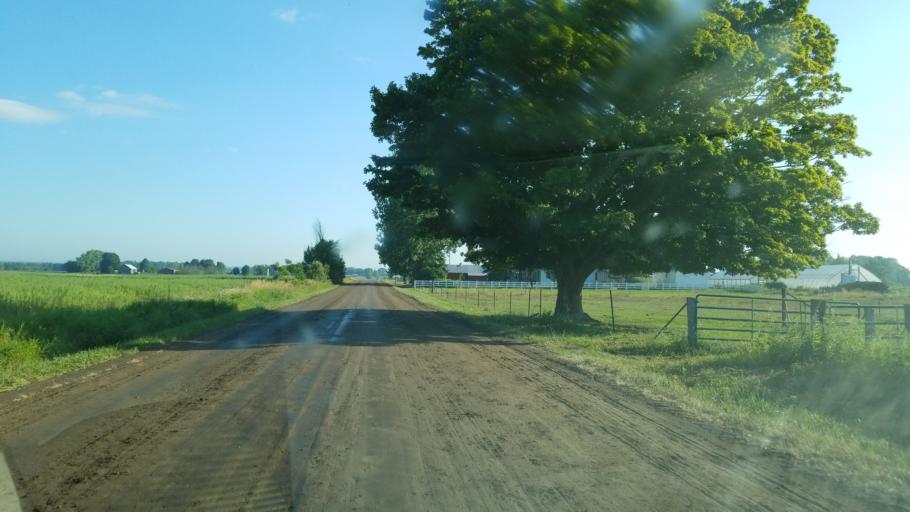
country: US
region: Michigan
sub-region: Mecosta County
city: Canadian Lakes
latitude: 43.5622
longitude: -85.3636
